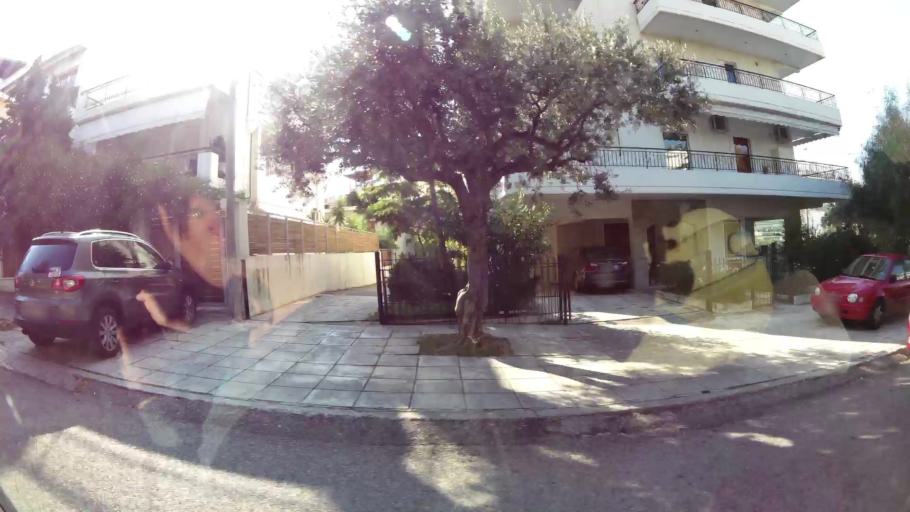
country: GR
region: Attica
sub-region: Nomarchia Athinas
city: Argyroupoli
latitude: 37.9209
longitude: 23.7522
